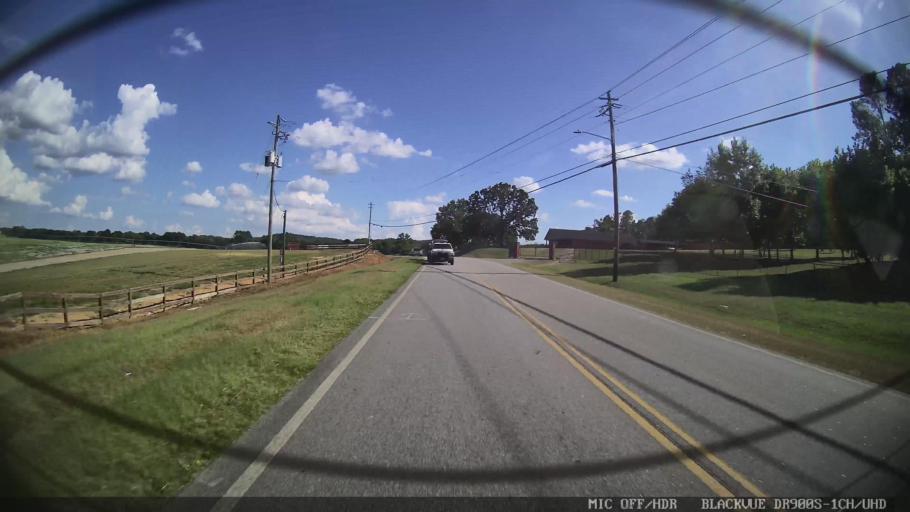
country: US
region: Georgia
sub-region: Bartow County
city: Euharlee
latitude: 34.0939
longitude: -84.9908
